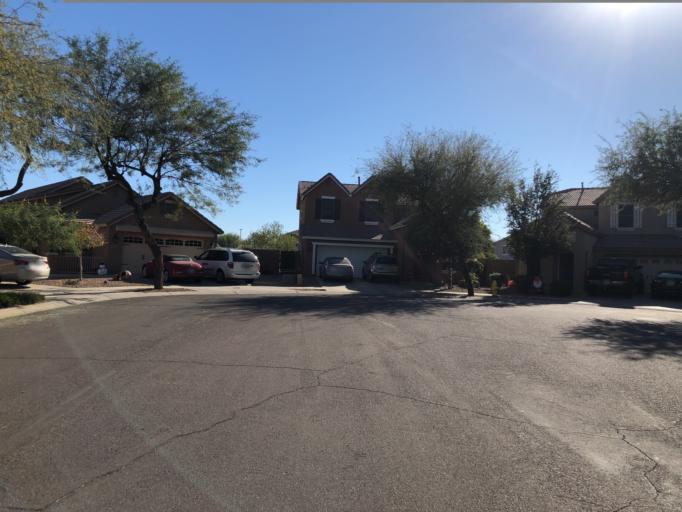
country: US
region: Arizona
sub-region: Maricopa County
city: Queen Creek
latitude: 33.2712
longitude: -111.7041
